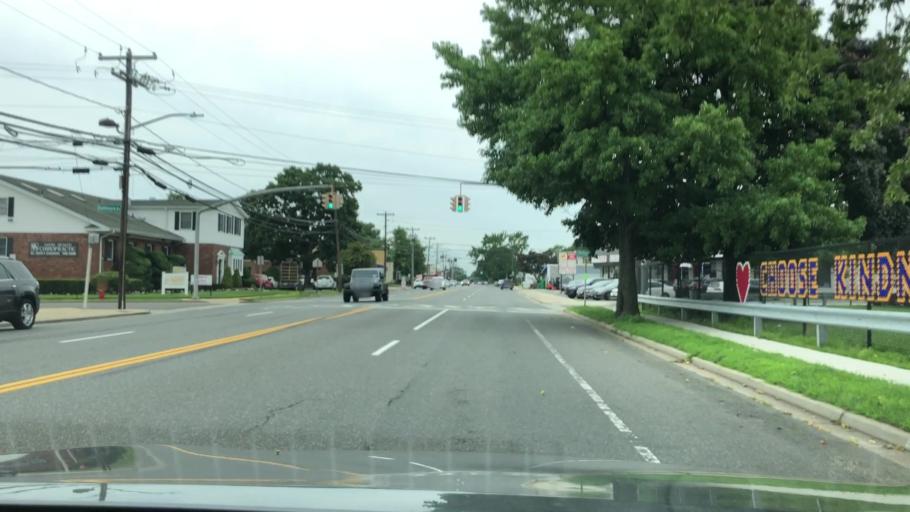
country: US
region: New York
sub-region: Nassau County
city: Massapequa
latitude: 40.6857
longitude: -73.4674
